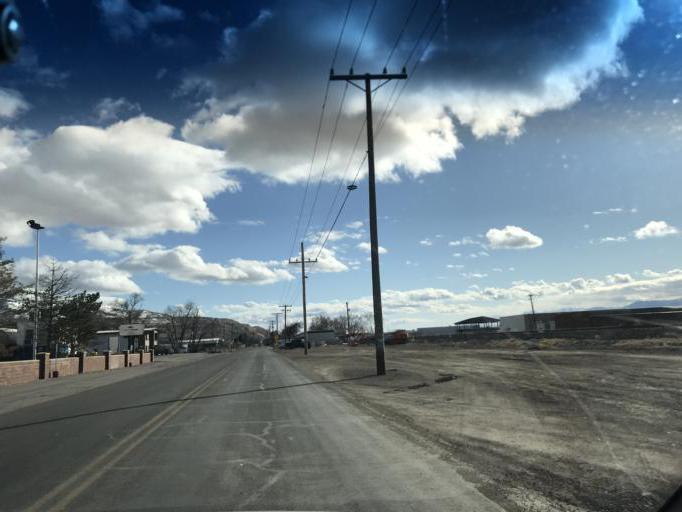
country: US
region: Utah
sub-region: Davis County
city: North Salt Lake
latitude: 40.8677
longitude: -111.9119
